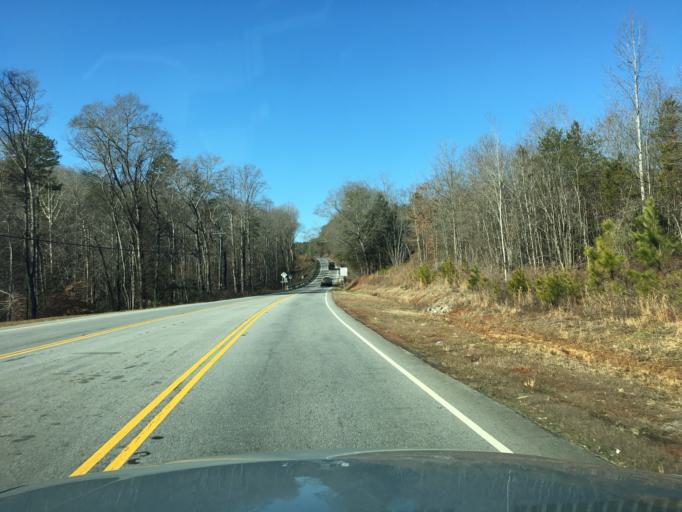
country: US
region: South Carolina
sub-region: Greenville County
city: Berea
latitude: 34.8864
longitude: -82.5027
